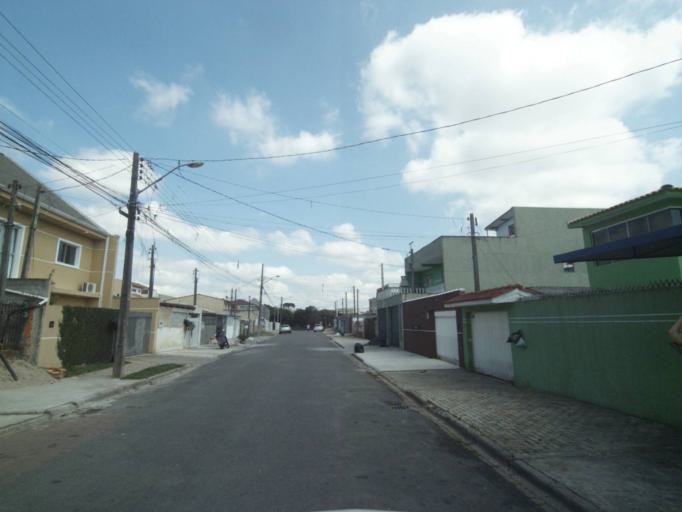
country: BR
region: Parana
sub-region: Sao Jose Dos Pinhais
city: Sao Jose dos Pinhais
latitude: -25.5399
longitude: -49.2659
